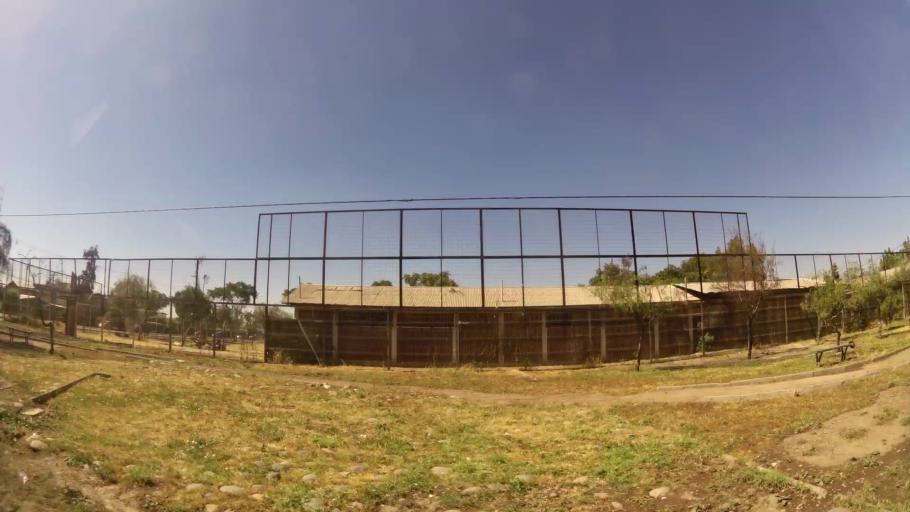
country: CL
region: Santiago Metropolitan
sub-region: Provincia de Maipo
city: San Bernardo
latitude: -33.5834
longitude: -70.6870
